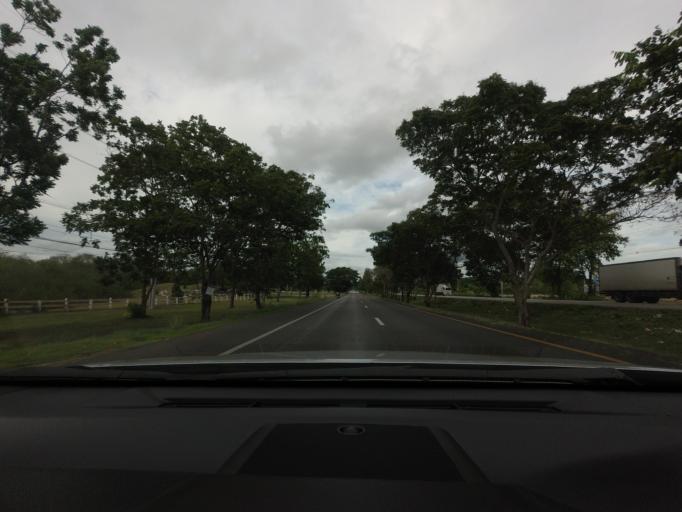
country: TH
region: Prachuap Khiri Khan
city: Hua Hin
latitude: 12.6831
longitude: 99.8912
